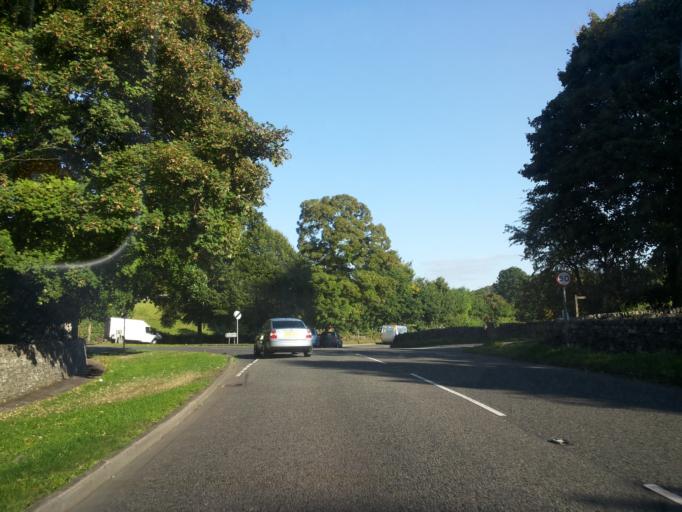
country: GB
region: England
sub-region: Derbyshire
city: Bakewell
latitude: 53.2352
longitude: -1.6945
